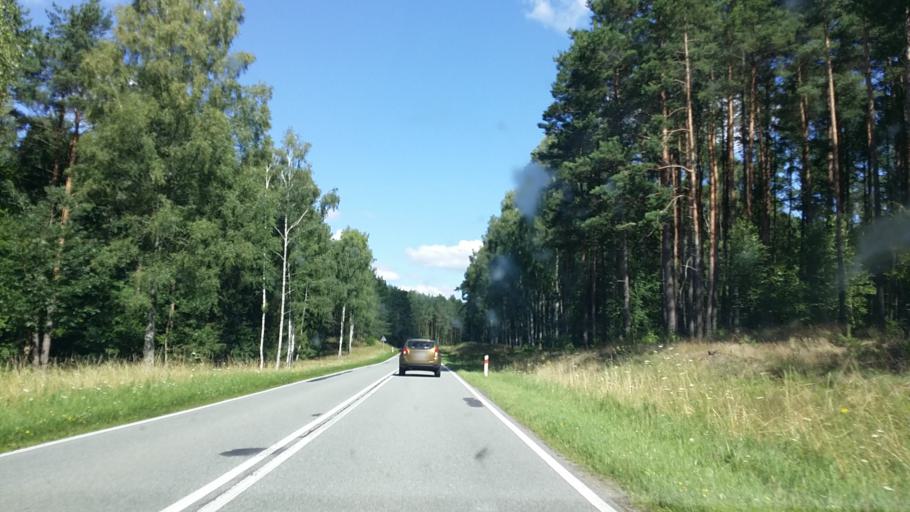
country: PL
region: West Pomeranian Voivodeship
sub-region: Powiat drawski
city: Drawsko Pomorskie
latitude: 53.4325
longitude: 15.8257
